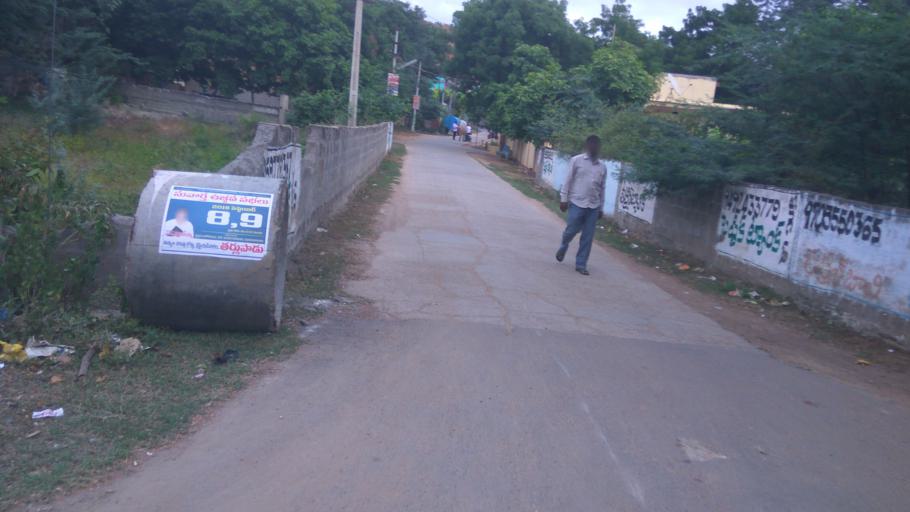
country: IN
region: Andhra Pradesh
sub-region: Prakasam
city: Cumbum
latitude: 15.5891
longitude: 79.1154
